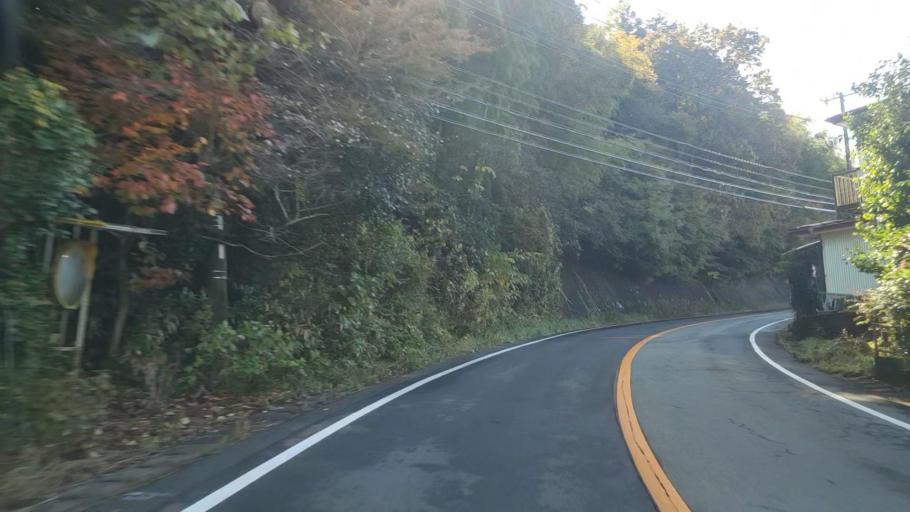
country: JP
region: Shizuoka
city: Atami
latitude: 35.0268
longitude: 139.0126
